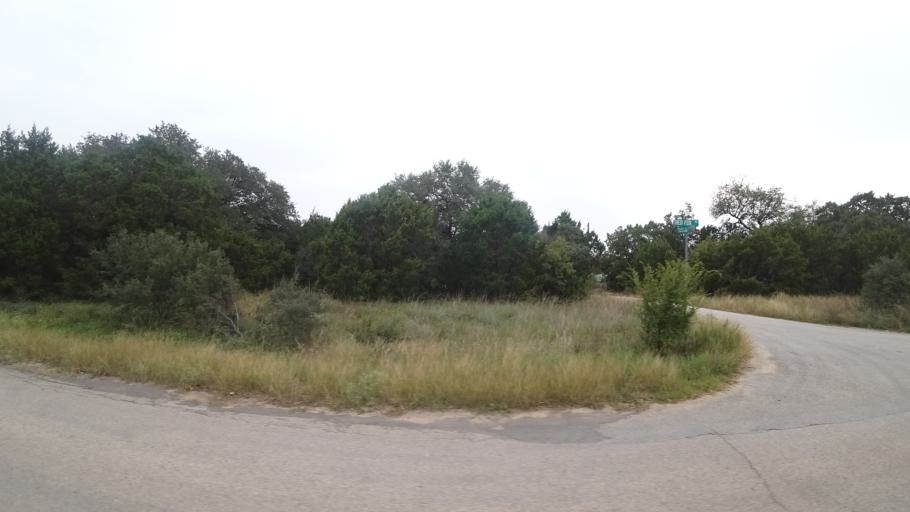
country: US
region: Texas
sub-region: Travis County
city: Hudson Bend
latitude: 30.3728
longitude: -97.9287
